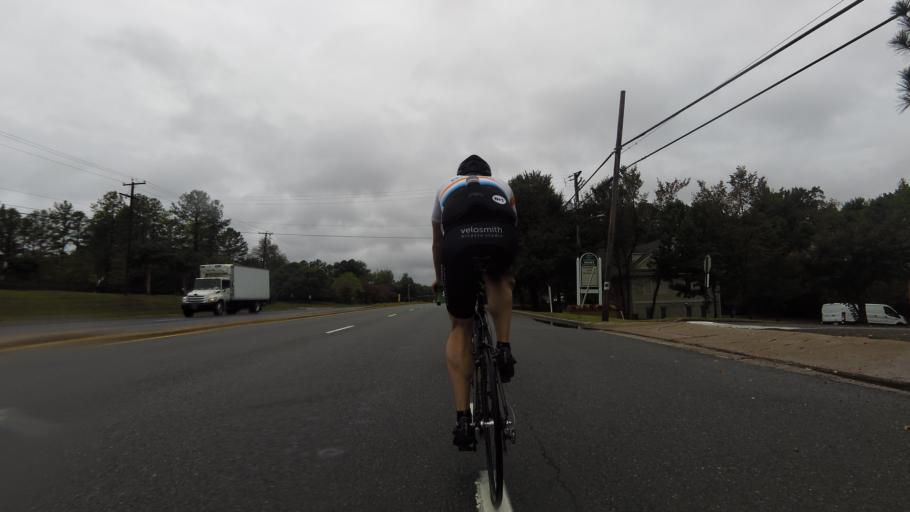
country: US
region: Virginia
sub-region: Henrico County
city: Tuckahoe
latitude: 37.5968
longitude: -77.6034
